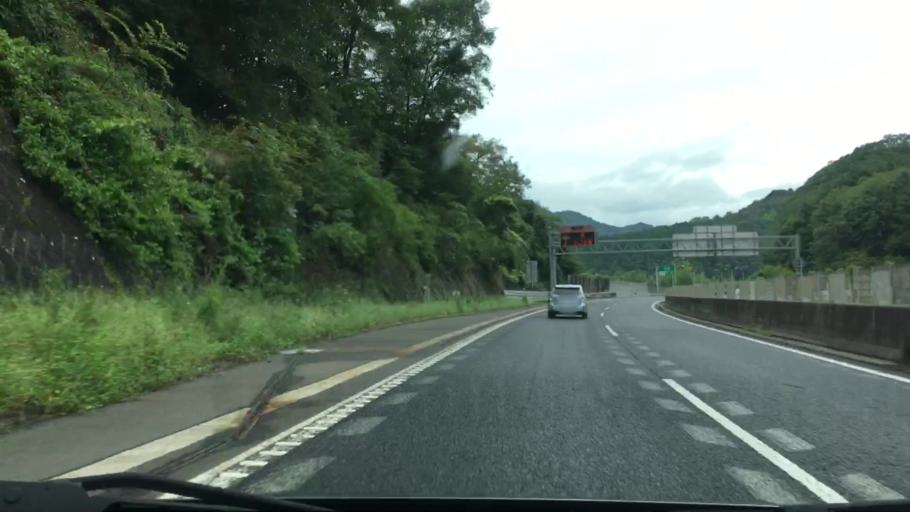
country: JP
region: Hyogo
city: Yamazakicho-nakabirose
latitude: 35.0200
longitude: 134.3762
